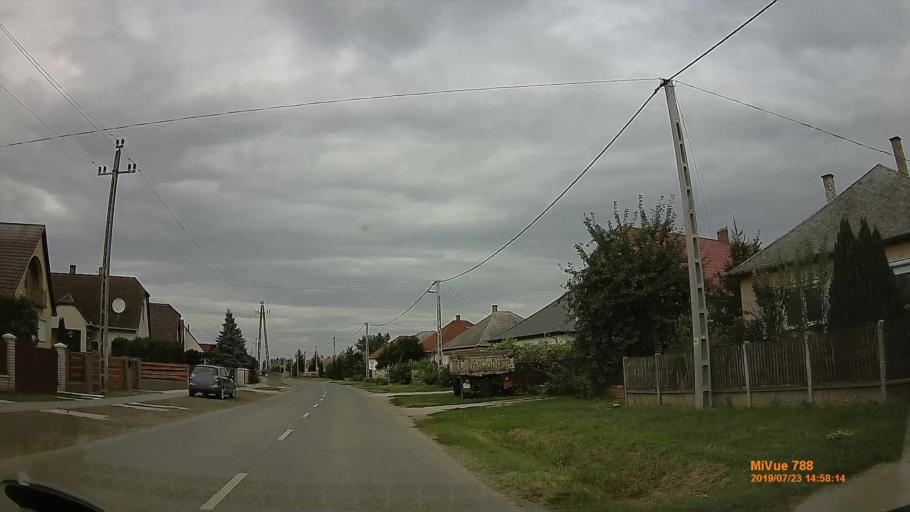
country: HU
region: Szabolcs-Szatmar-Bereg
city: Nyiregyhaza
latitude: 47.9116
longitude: 21.6749
